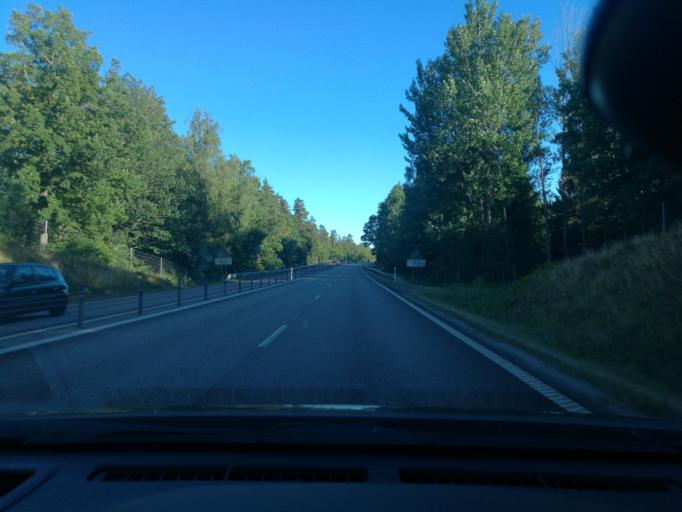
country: SE
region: Kalmar
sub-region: Monsteras Kommun
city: Timmernabben
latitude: 56.8871
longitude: 16.3821
